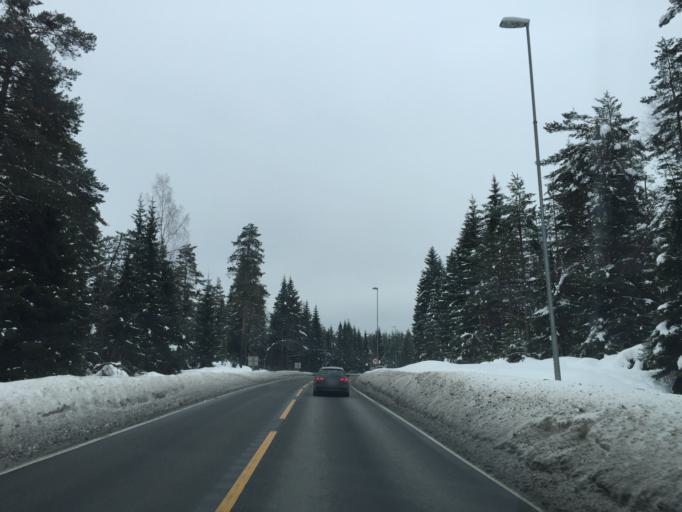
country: NO
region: Hedmark
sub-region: Loten
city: Loten
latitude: 60.8686
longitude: 11.4284
